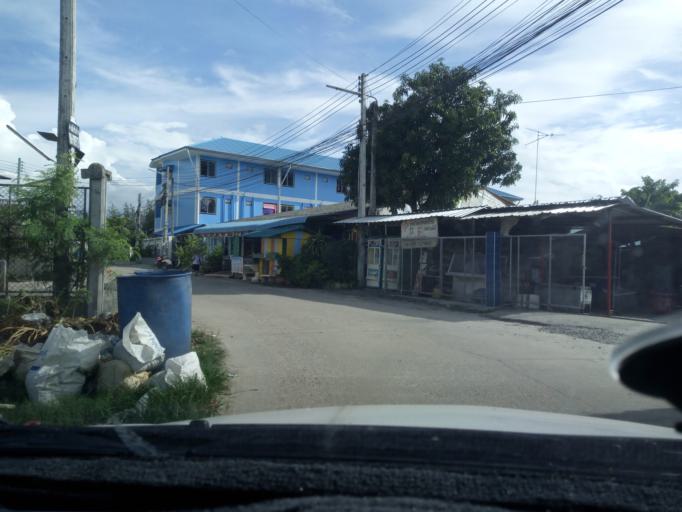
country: TH
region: Chon Buri
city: Phan Thong
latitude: 13.4188
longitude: 101.0609
